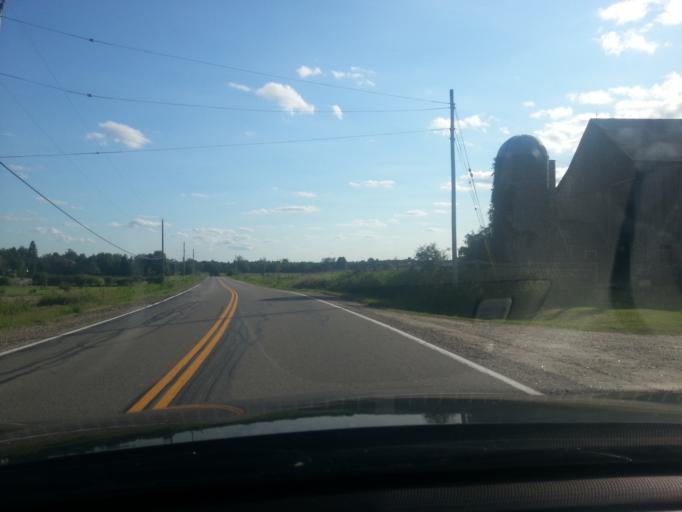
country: CA
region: Ontario
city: Carleton Place
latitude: 45.0794
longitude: -76.2630
